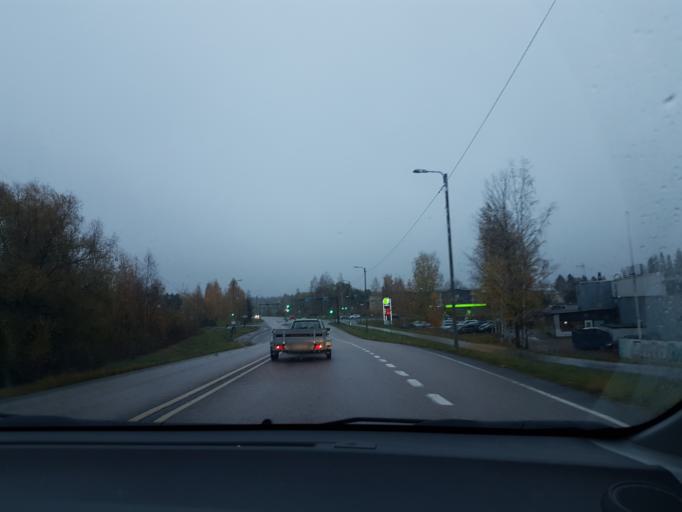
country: FI
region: Uusimaa
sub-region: Helsinki
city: Tuusula
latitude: 60.4133
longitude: 25.0491
